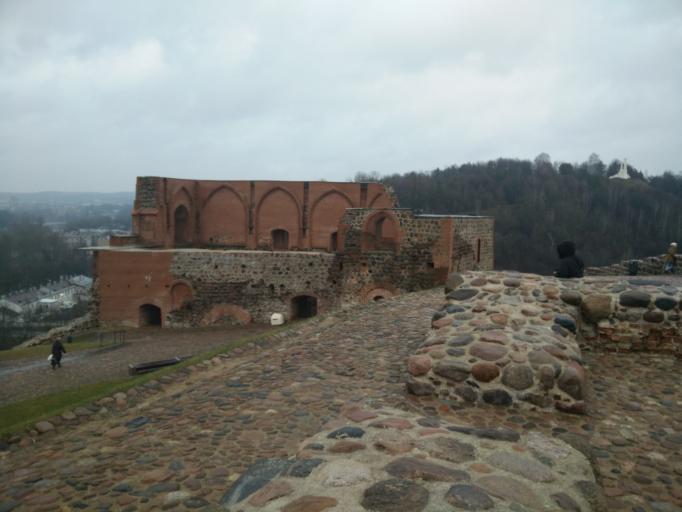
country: LT
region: Vilnius County
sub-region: Vilnius
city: Vilnius
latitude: 54.6867
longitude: 25.2914
